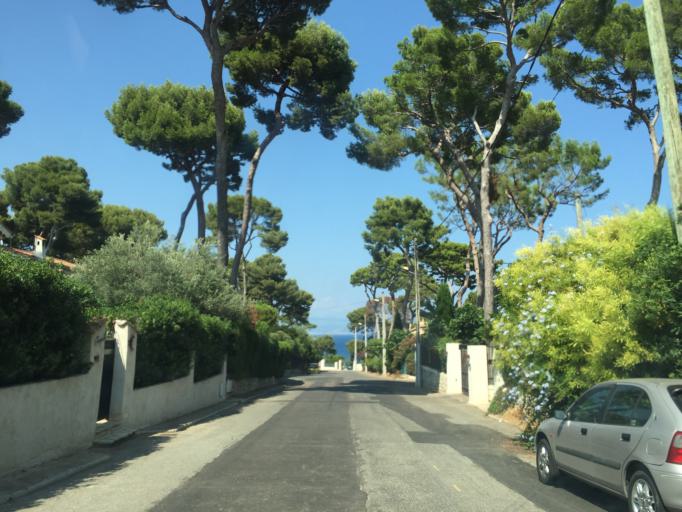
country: FR
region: Provence-Alpes-Cote d'Azur
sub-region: Departement des Alpes-Maritimes
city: Antibes
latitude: 43.5635
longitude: 7.1357
